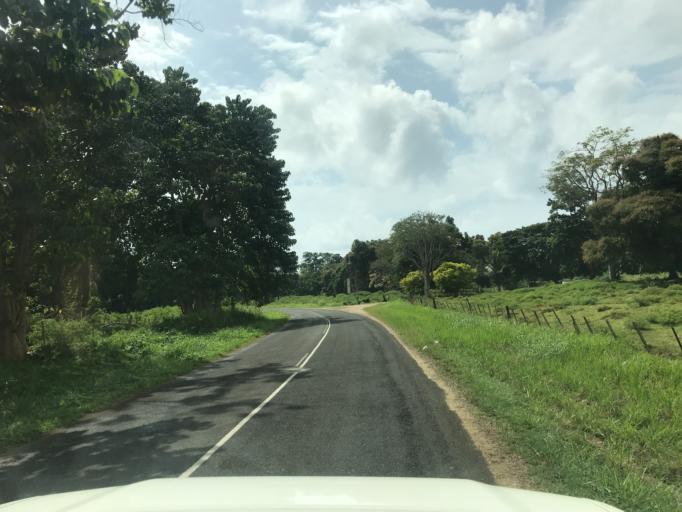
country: VU
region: Sanma
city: Luganville
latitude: -15.4823
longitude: 167.2012
